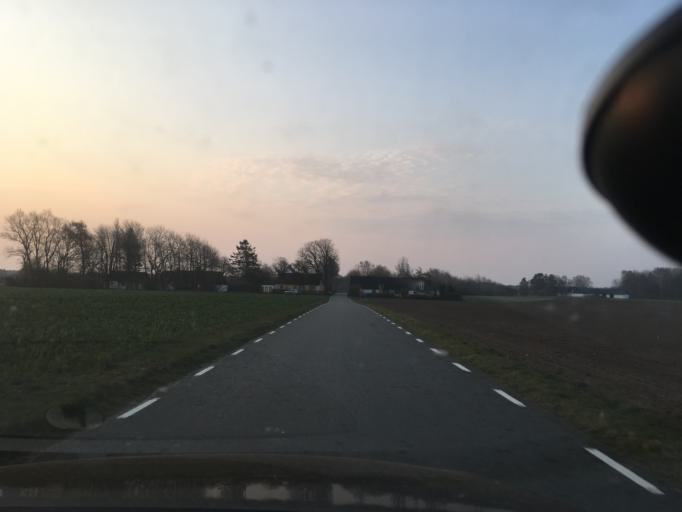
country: SE
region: Skane
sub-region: Ystads Kommun
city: Kopingebro
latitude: 55.4034
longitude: 14.1610
